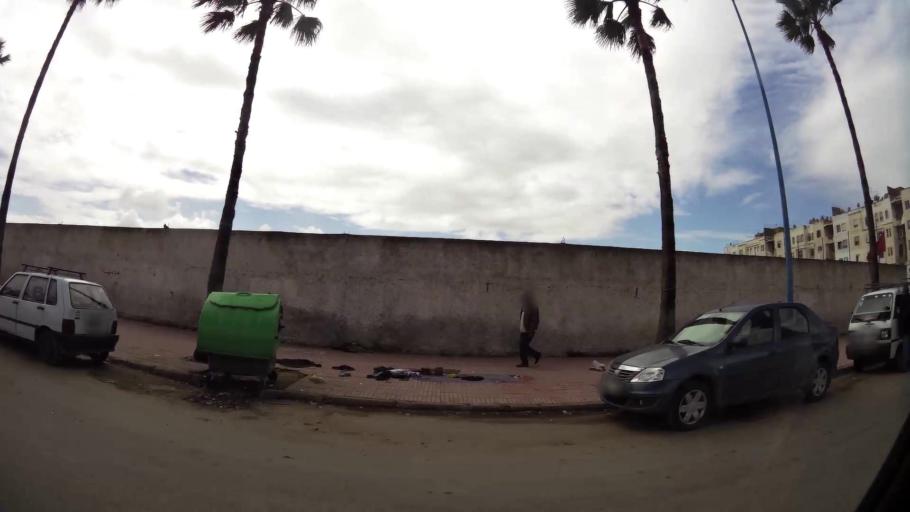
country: MA
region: Grand Casablanca
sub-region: Casablanca
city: Casablanca
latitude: 33.5705
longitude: -7.6806
